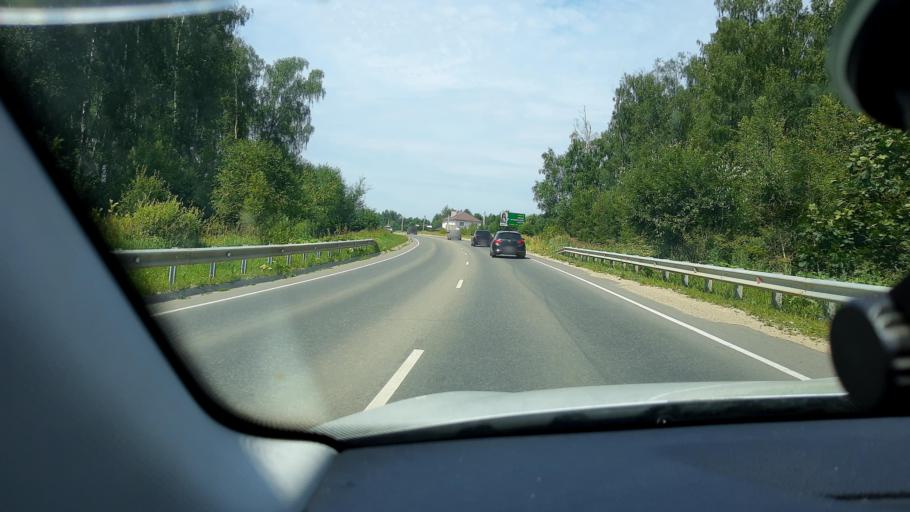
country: RU
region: Tula
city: Zaokskiy
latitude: 54.7441
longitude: 37.4160
